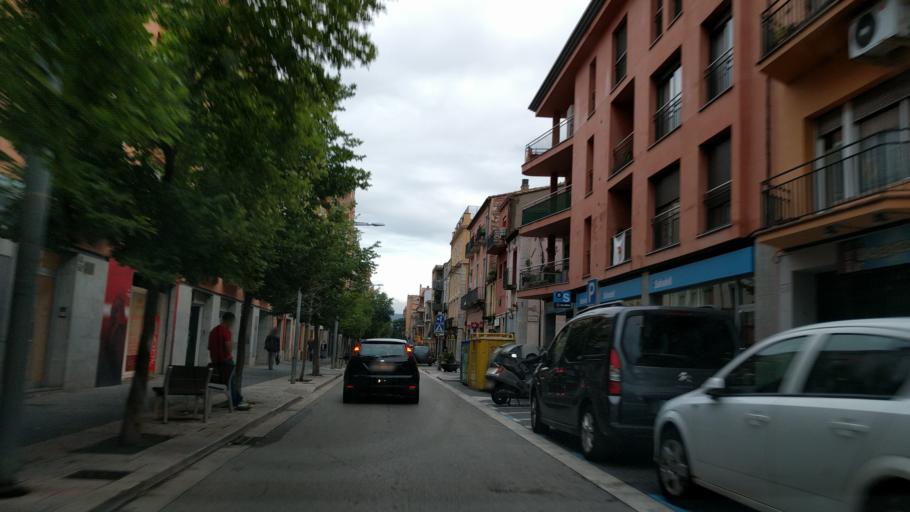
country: ES
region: Catalonia
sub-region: Provincia de Girona
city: Salt
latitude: 41.9761
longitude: 2.7978
